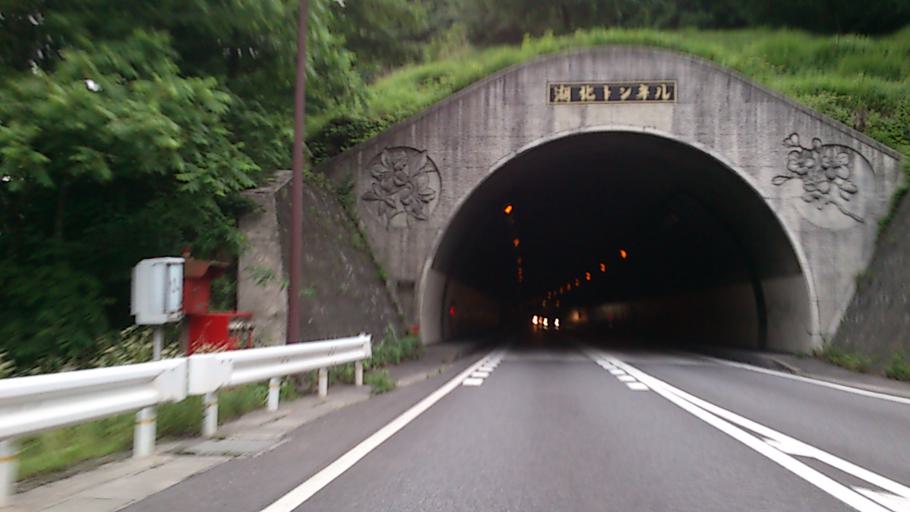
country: JP
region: Nagano
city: Okaya
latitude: 36.0972
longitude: 138.0861
